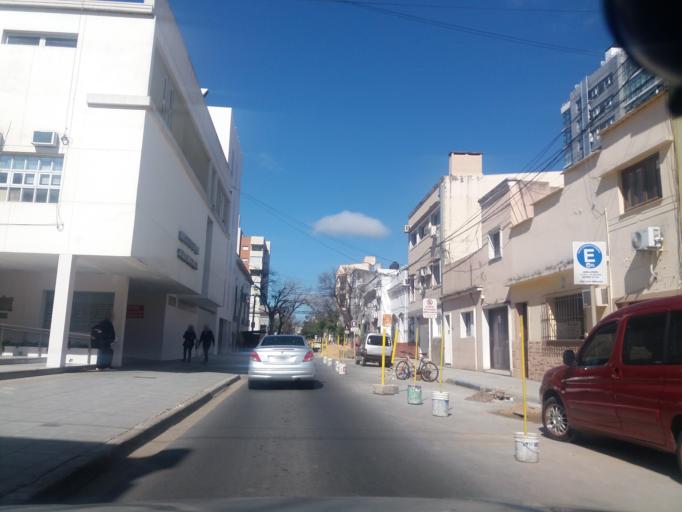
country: AR
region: Corrientes
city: Corrientes
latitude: -27.4714
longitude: -58.8348
